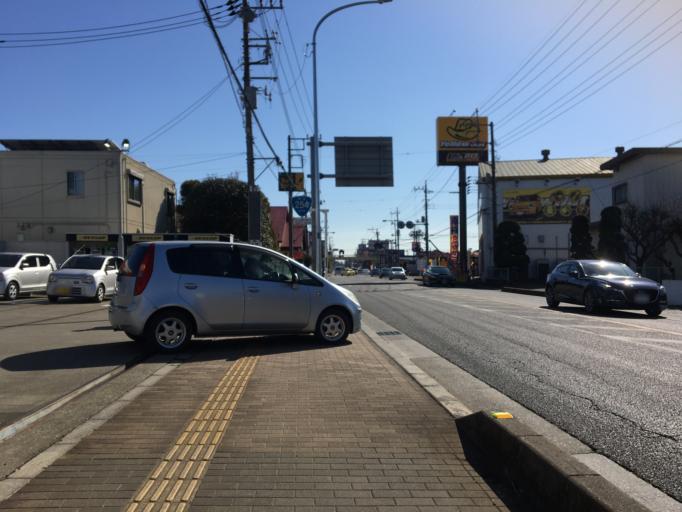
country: JP
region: Saitama
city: Kamifukuoka
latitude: 35.8615
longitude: 139.5117
